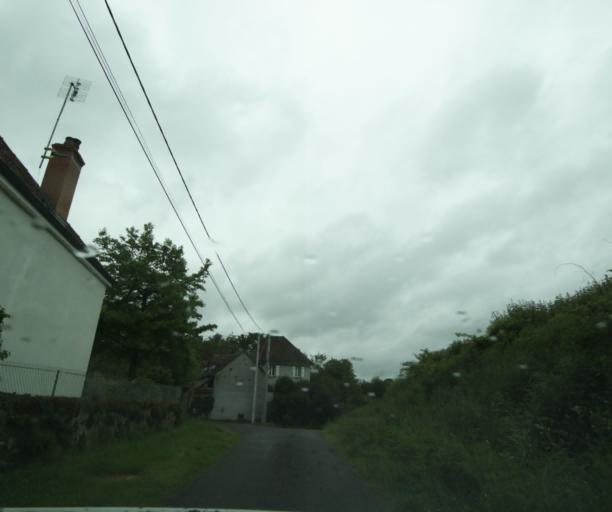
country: FR
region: Bourgogne
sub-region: Departement de Saone-et-Loire
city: Palinges
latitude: 46.4946
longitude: 4.2500
